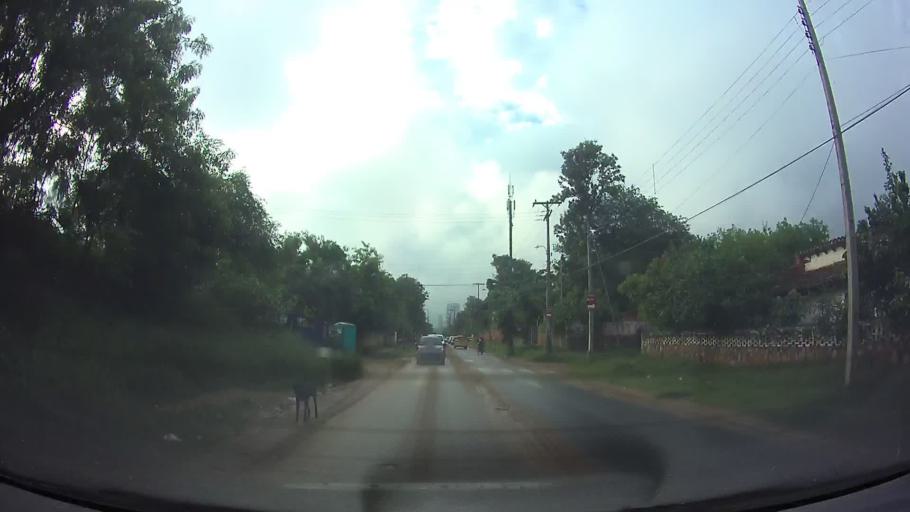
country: PY
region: Asuncion
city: Asuncion
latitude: -25.2482
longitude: -57.5862
